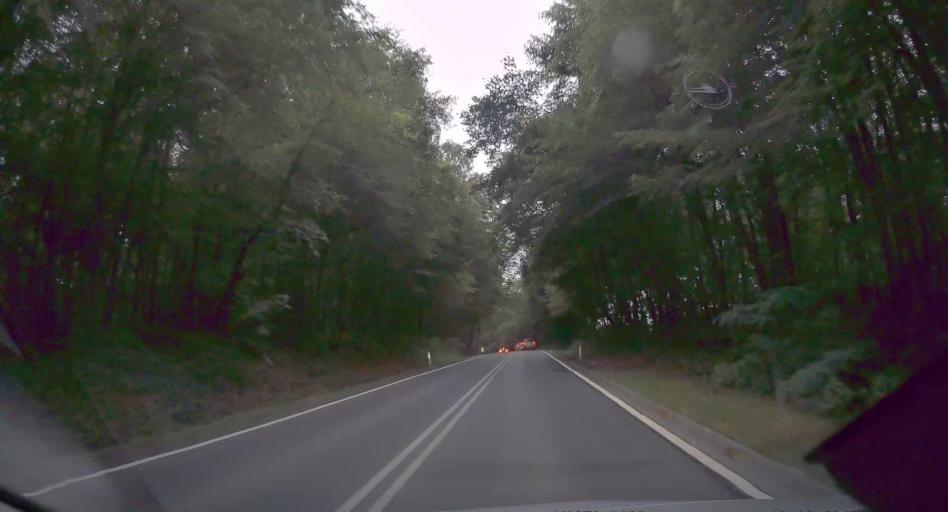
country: PL
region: Lesser Poland Voivodeship
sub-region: Powiat krakowski
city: Slomniki
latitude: 50.1735
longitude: 20.0952
